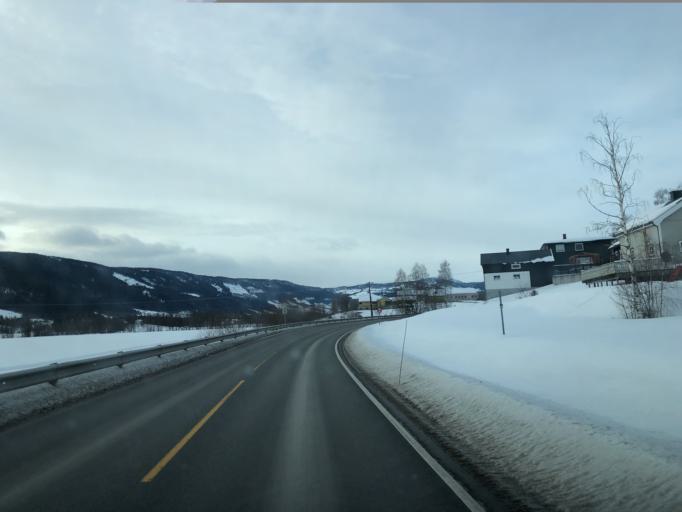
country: NO
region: Oppland
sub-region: Gausdal
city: Segalstad bru
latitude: 61.2310
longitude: 10.2141
